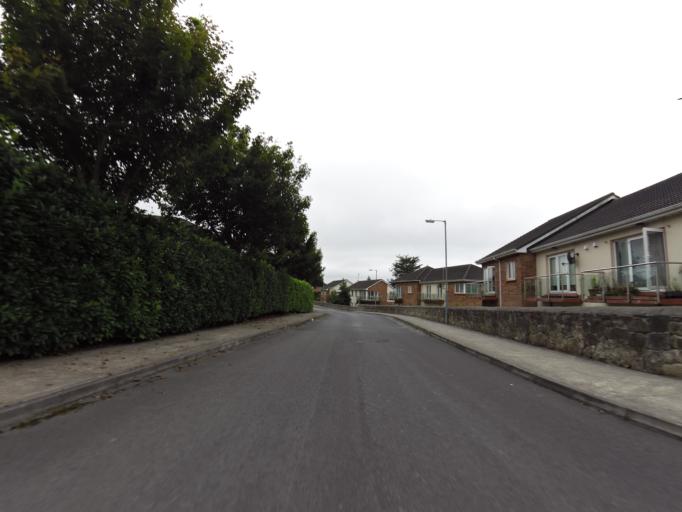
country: IE
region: Connaught
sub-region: County Galway
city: Loughrea
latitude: 53.2043
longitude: -8.5611
